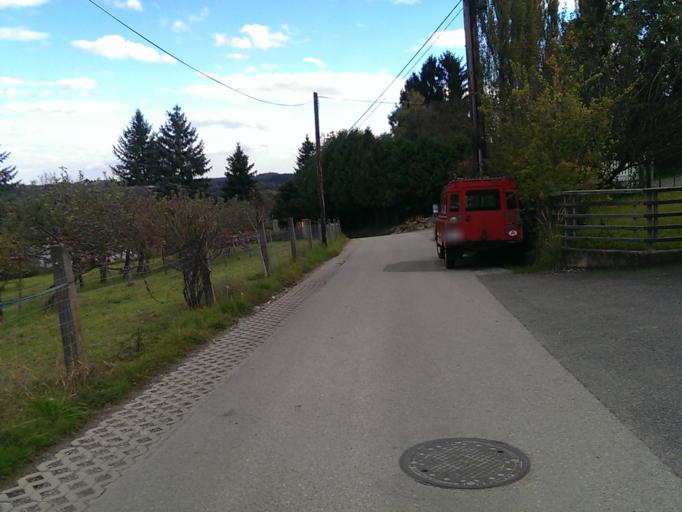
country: AT
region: Styria
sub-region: Politischer Bezirk Graz-Umgebung
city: Raaba
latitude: 47.0465
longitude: 15.4903
